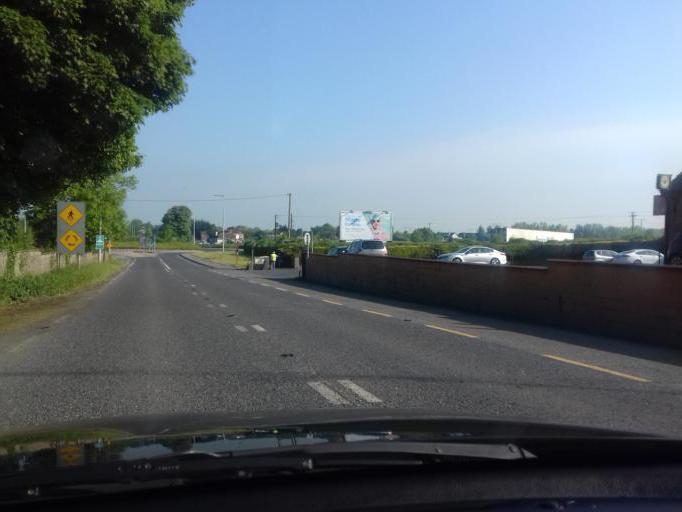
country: IE
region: Leinster
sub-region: Dublin City
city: Finglas
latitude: 53.4331
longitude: -6.3330
